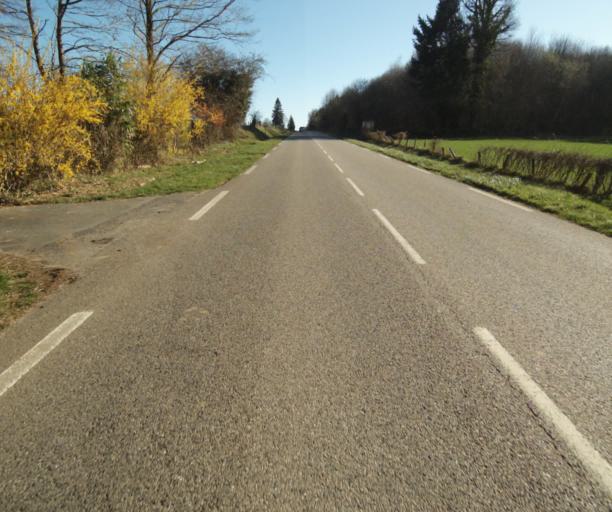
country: FR
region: Limousin
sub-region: Departement de la Correze
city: Seilhac
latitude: 45.3866
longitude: 1.7219
